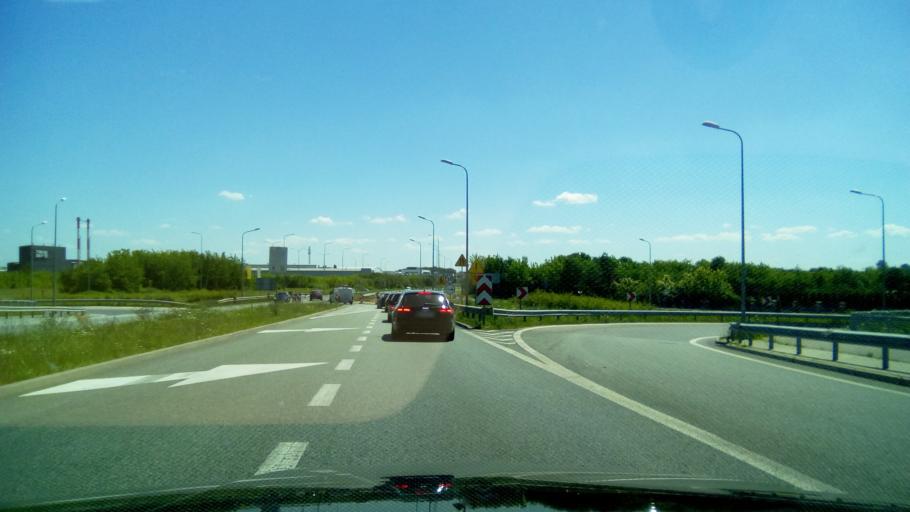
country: PL
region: Masovian Voivodeship
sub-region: Radom
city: Radom
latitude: 51.4191
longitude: 21.1884
